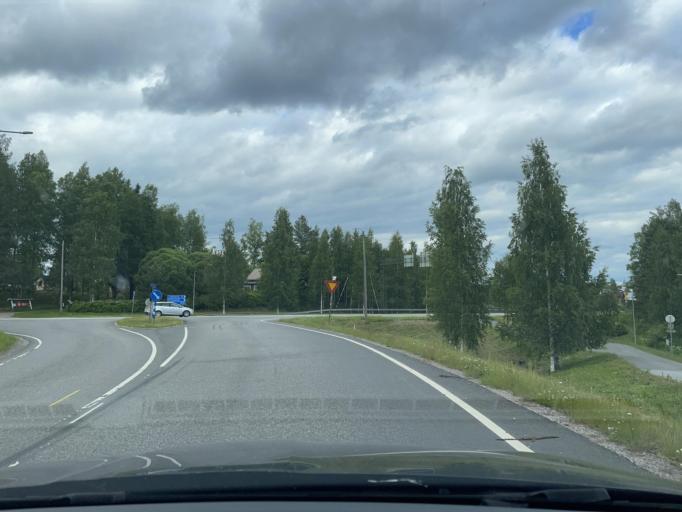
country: FI
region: Central Finland
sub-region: Jyvaeskylae
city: Petaejaevesi
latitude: 62.2470
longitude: 25.1712
